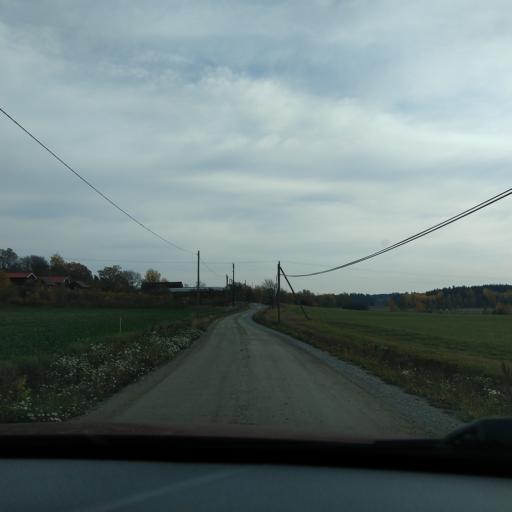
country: SE
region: Stockholm
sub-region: Vallentuna Kommun
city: Vallentuna
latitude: 59.5300
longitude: 18.0073
